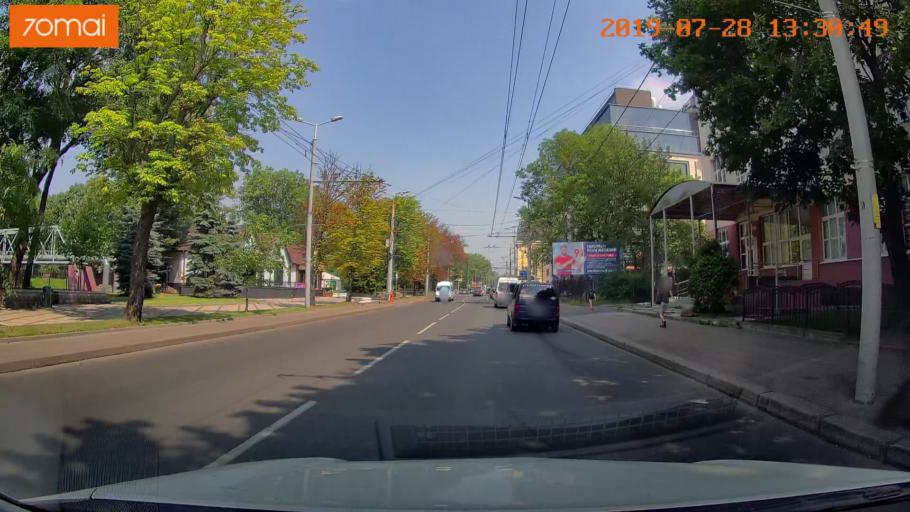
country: RU
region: Kaliningrad
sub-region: Gorod Kaliningrad
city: Kaliningrad
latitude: 54.7172
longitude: 20.4957
